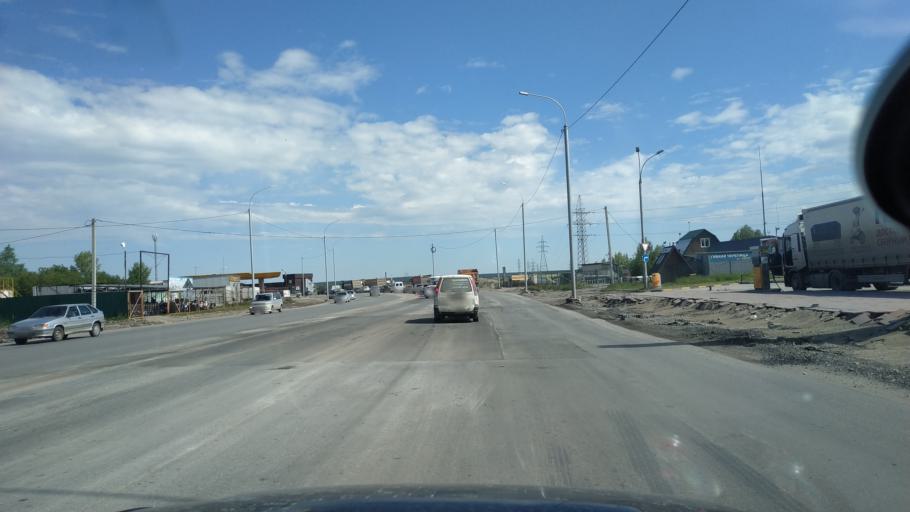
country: RU
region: Novosibirsk
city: Kudryashovskiy
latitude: 55.0218
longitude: 82.8144
